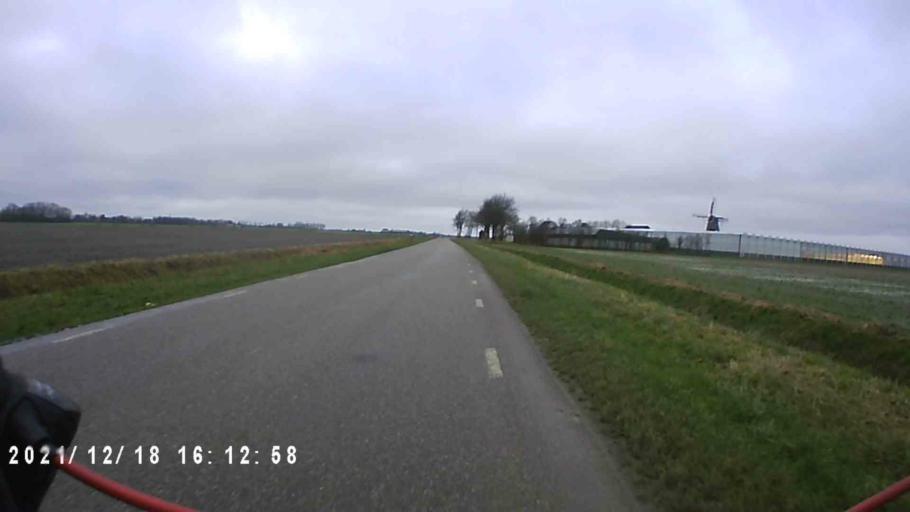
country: NL
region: Friesland
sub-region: Gemeente Dongeradeel
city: Anjum
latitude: 53.3668
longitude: 6.0687
